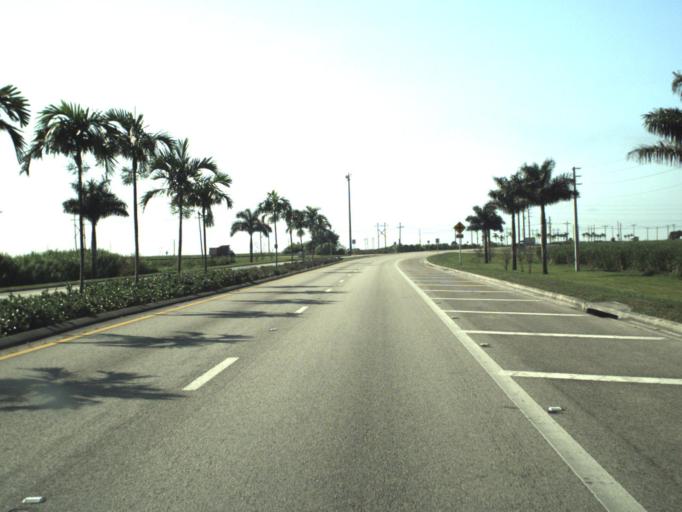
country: US
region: Florida
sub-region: Palm Beach County
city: South Bay
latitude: 26.6599
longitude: -80.7139
